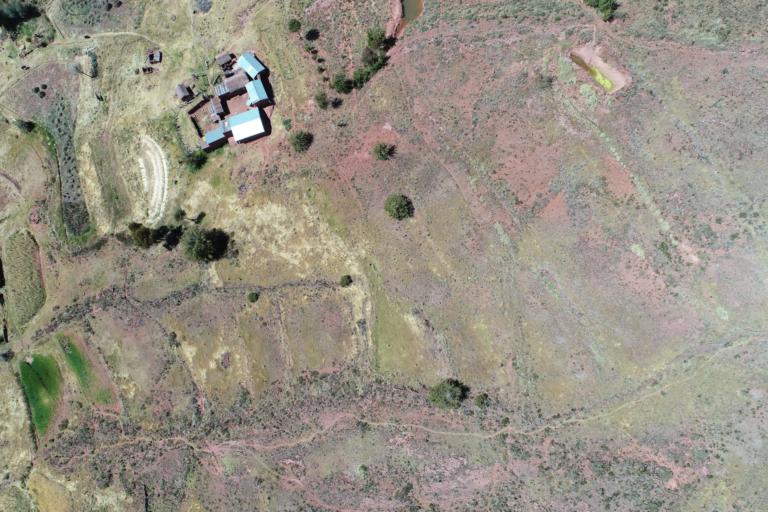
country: BO
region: La Paz
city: Tiahuanaco
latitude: -16.6072
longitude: -68.7650
